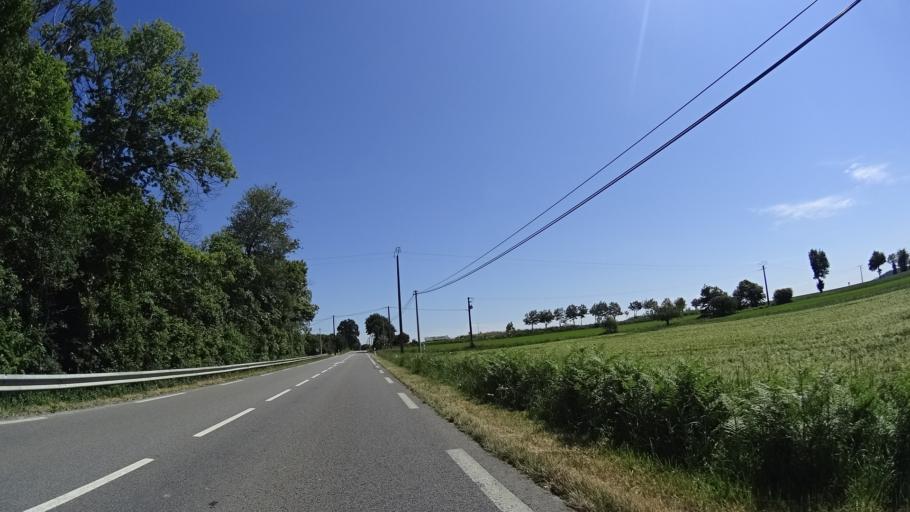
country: FR
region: Brittany
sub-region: Departement d'Ille-et-Vilaine
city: Bain-de-Bretagne
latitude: 47.8360
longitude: -1.7351
